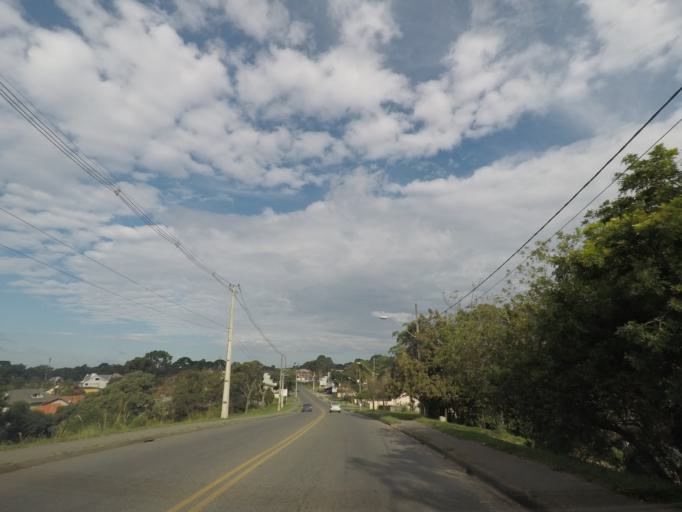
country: BR
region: Parana
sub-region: Sao Jose Dos Pinhais
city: Sao Jose dos Pinhais
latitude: -25.5635
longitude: -49.2904
